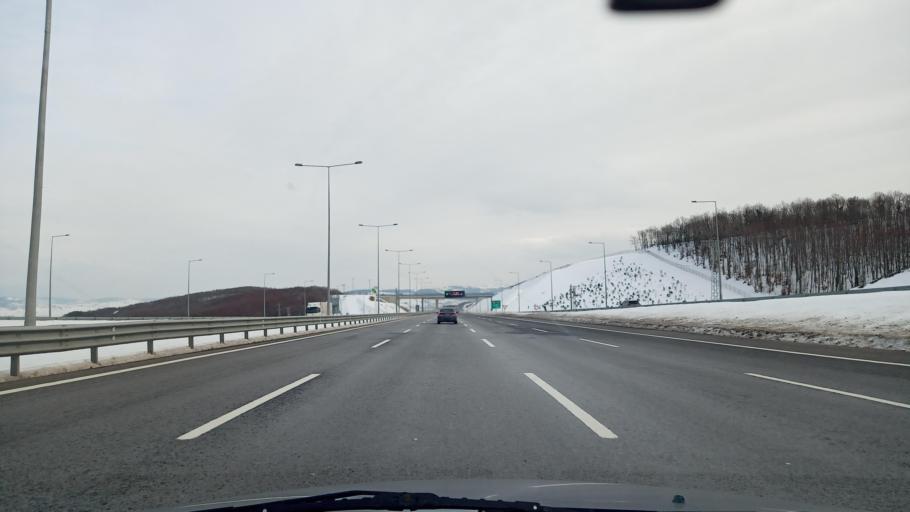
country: TR
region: Kocaeli
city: Korfez
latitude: 40.8894
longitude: 29.7170
